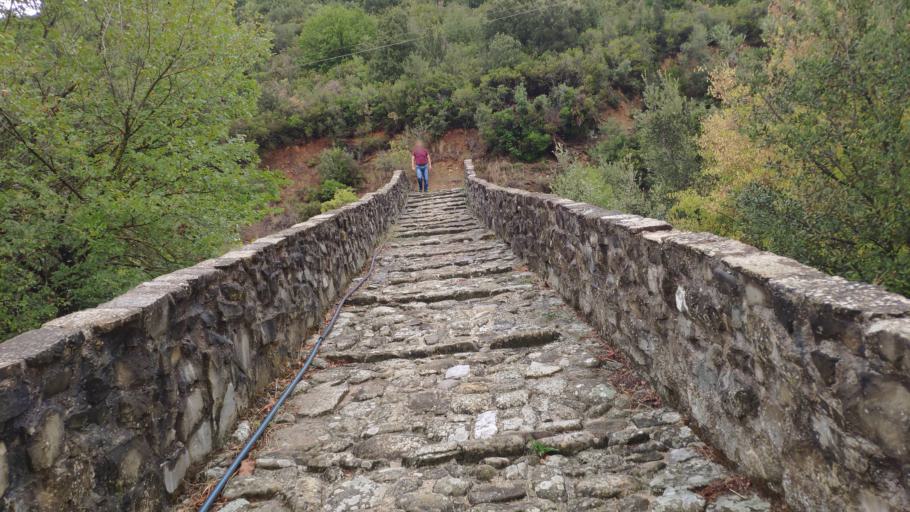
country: GR
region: West Greece
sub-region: Nomos Aitolias kai Akarnanias
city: Sardinia
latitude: 38.9259
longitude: 21.3573
